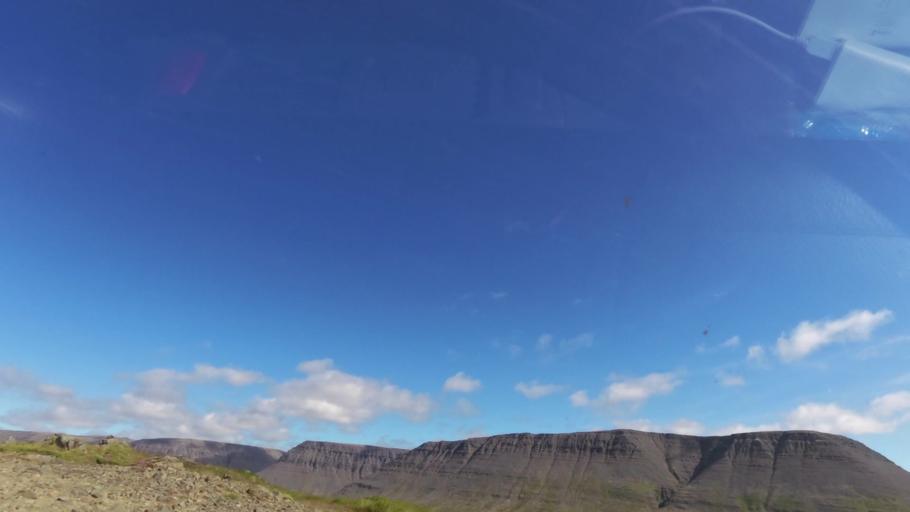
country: IS
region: West
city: Olafsvik
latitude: 65.6246
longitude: -23.8958
